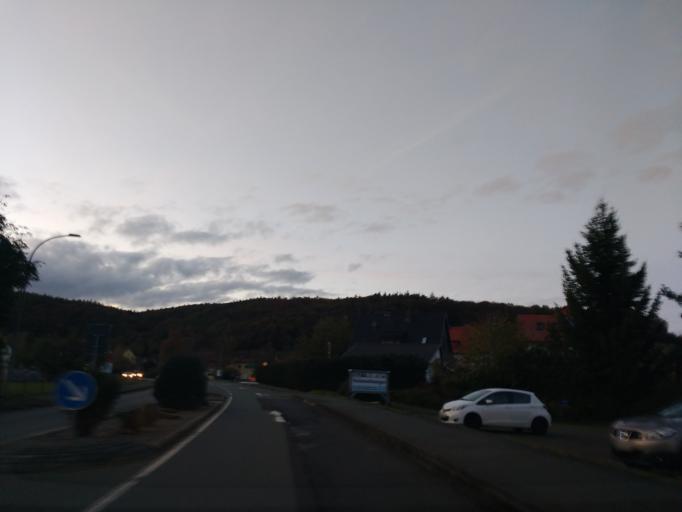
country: DE
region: Hesse
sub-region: Regierungsbezirk Kassel
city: Waldeck
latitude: 51.1672
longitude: 9.0856
